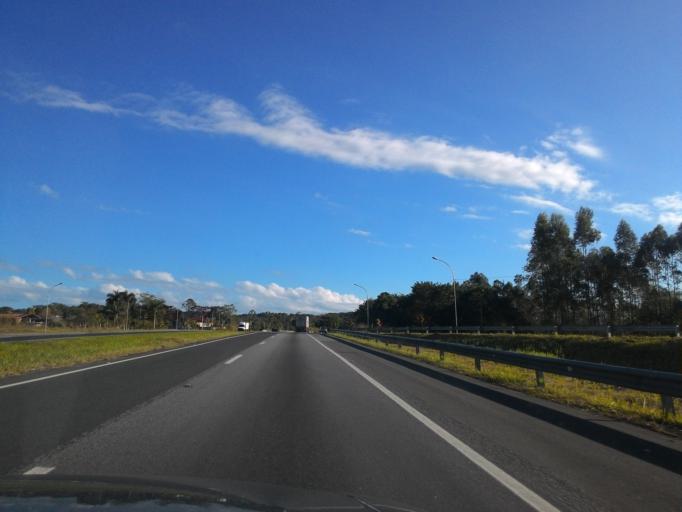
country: BR
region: Sao Paulo
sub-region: Pariquera-Acu
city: Pariquera Acu
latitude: -24.6455
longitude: -47.9201
